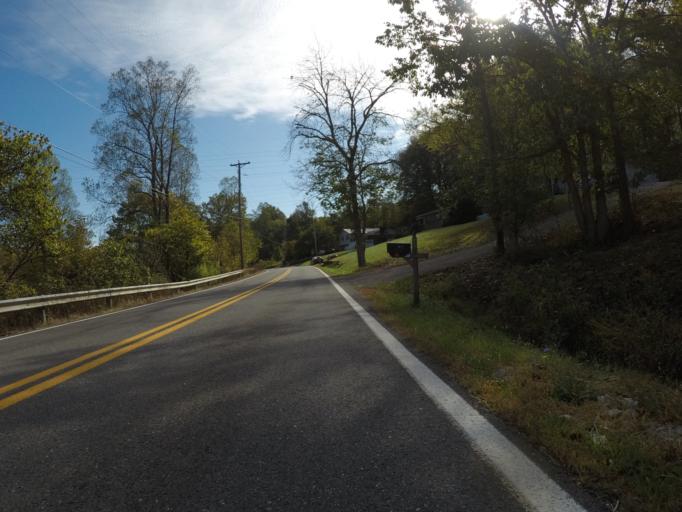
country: US
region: Ohio
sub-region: Lawrence County
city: Burlington
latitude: 38.3564
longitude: -82.5234
